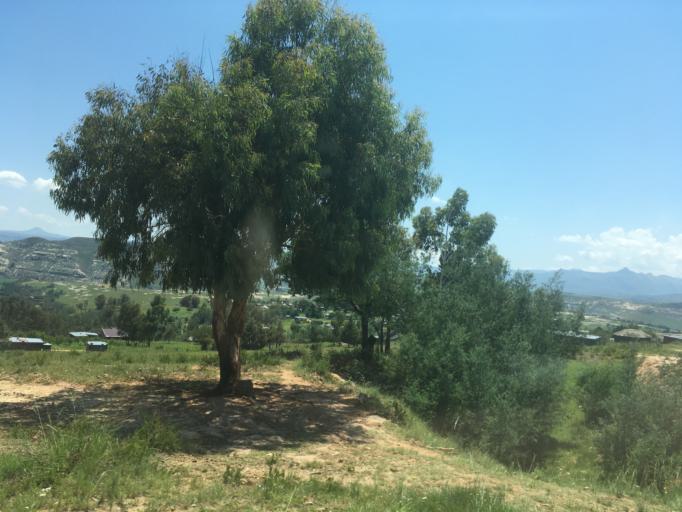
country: LS
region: Butha-Buthe
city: Butha-Buthe
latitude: -28.7279
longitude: 28.3622
